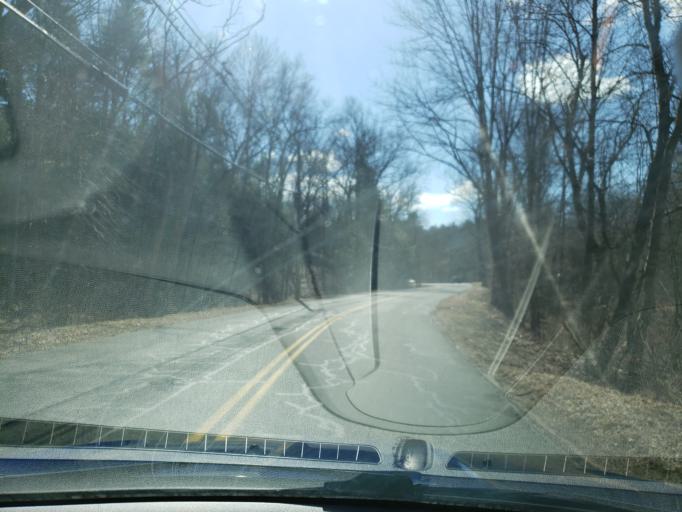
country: US
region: Connecticut
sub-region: Hartford County
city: Hazardville
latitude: 41.9810
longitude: -72.5418
